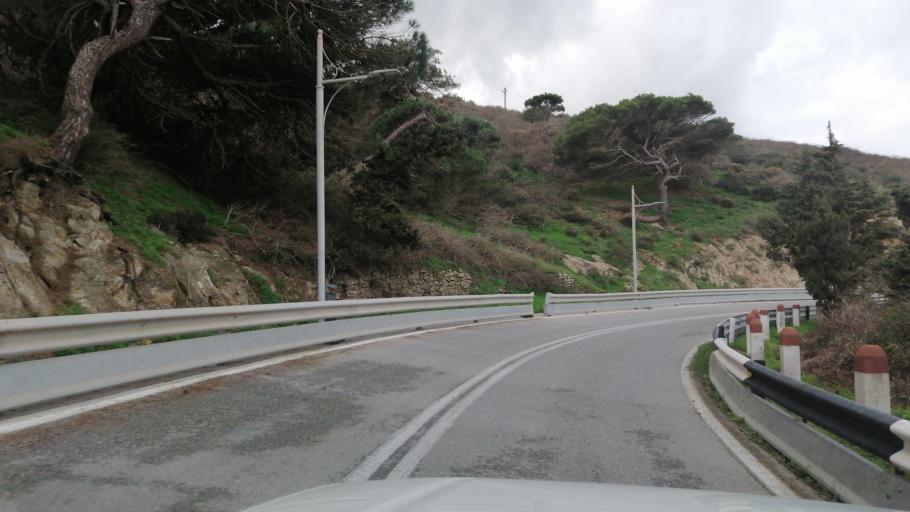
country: ES
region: Ceuta
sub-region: Ceuta
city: Ceuta
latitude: 35.8976
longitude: -5.2858
